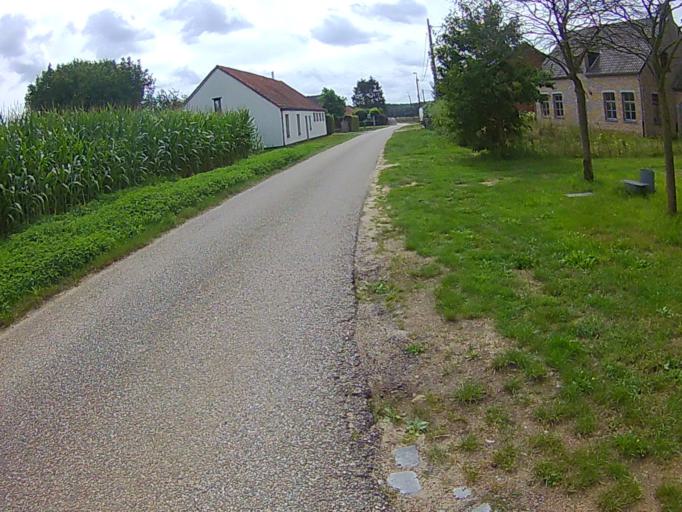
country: BE
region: Flanders
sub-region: Provincie Antwerpen
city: Lille
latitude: 51.2098
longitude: 4.8121
